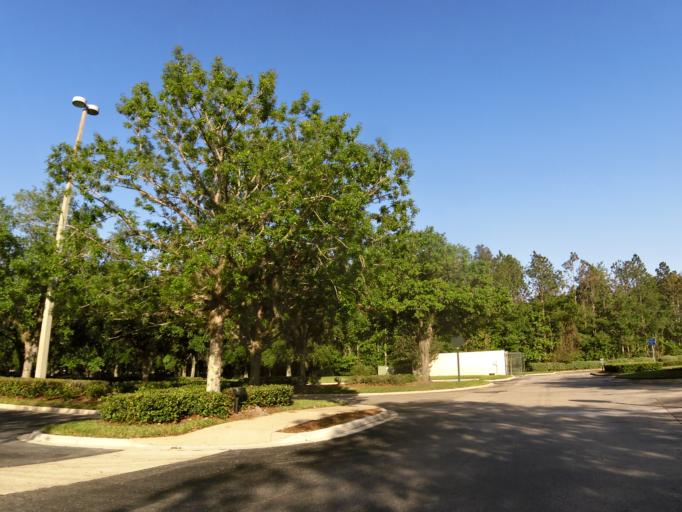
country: US
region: Florida
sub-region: Saint Johns County
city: Villano Beach
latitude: 29.9914
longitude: -81.4668
